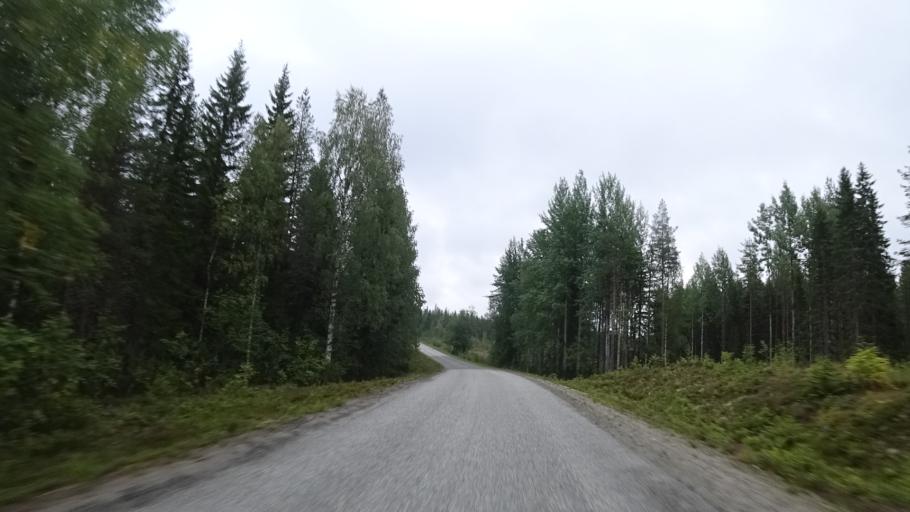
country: FI
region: North Karelia
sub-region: Joensuu
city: Ilomantsi
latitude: 63.2275
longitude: 30.8312
